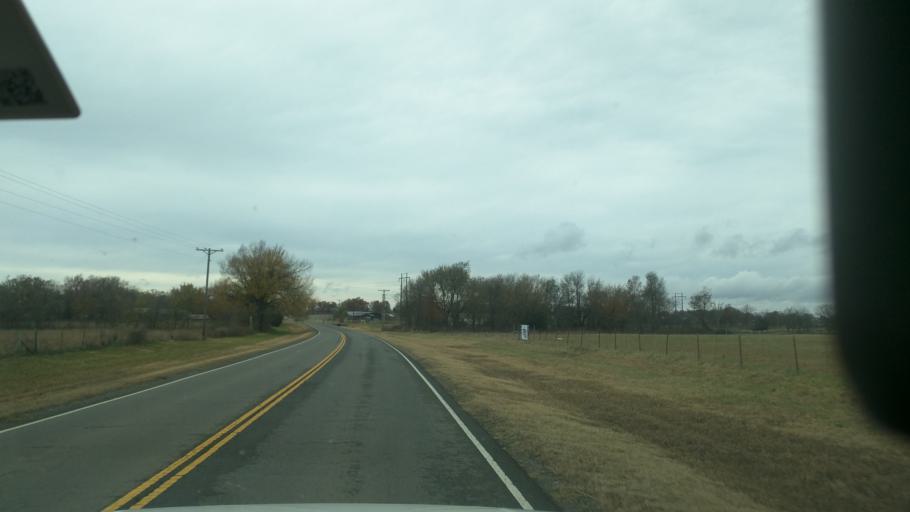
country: US
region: Oklahoma
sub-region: Adair County
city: Stilwell
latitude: 35.8942
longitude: -94.7782
